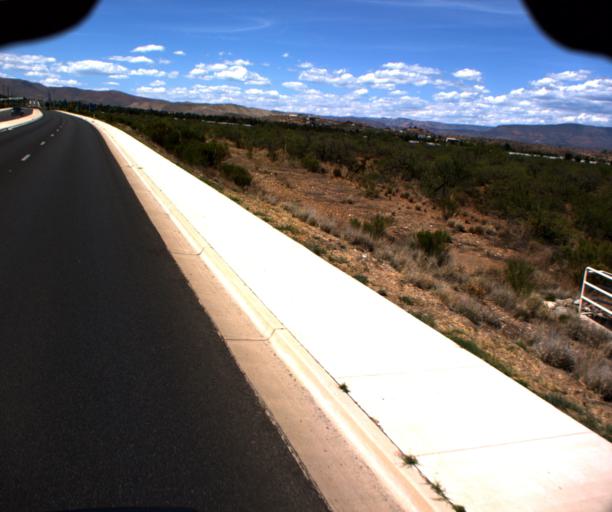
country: US
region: Arizona
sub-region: Yavapai County
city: Cottonwood
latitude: 34.7437
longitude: -112.0411
